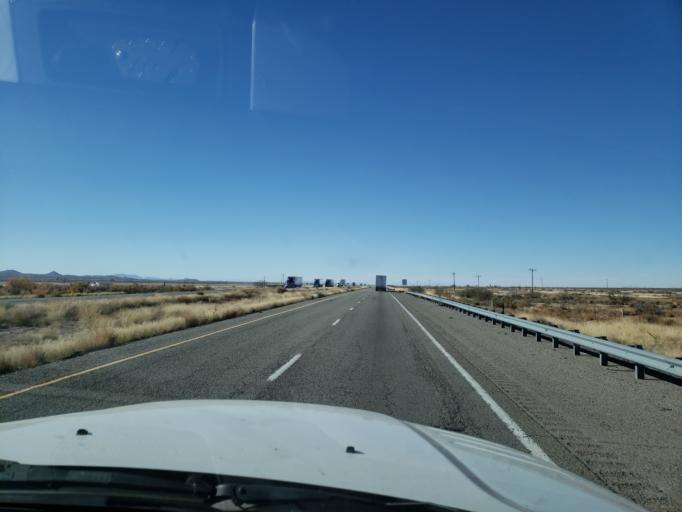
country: US
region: New Mexico
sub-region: Hidalgo County
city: Lordsburg
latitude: 32.3183
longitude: -108.6175
